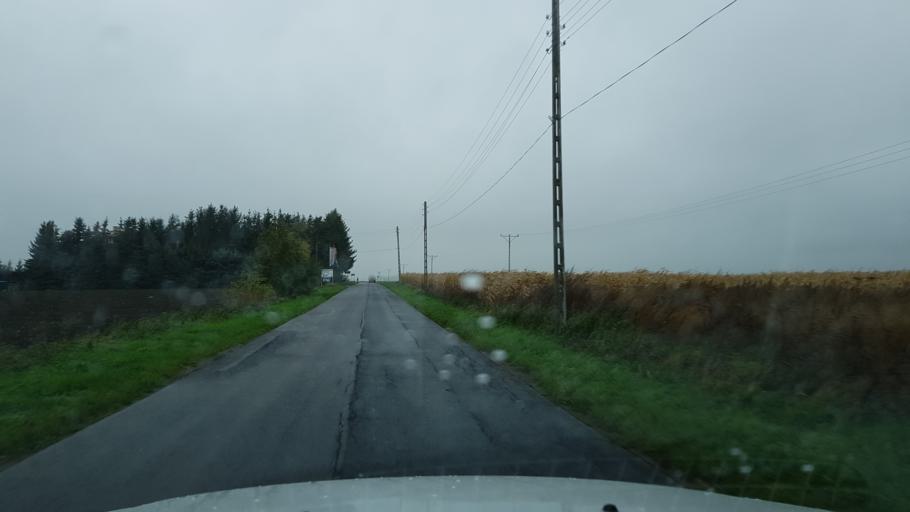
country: PL
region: West Pomeranian Voivodeship
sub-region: Powiat pyrzycki
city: Pyrzyce
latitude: 53.1555
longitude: 14.8711
